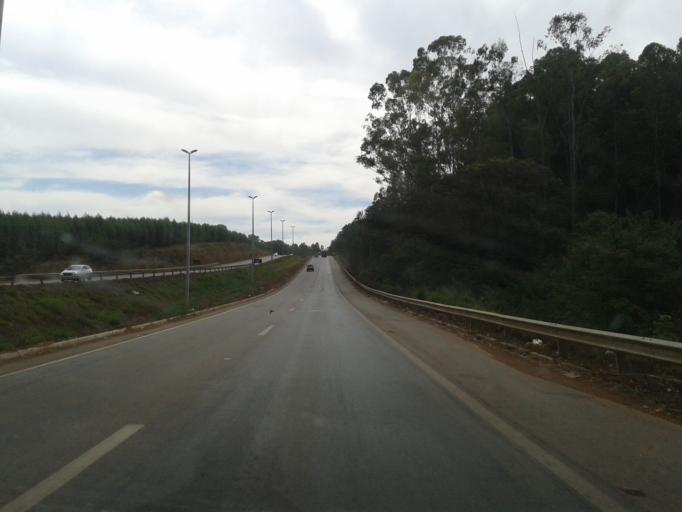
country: BR
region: Goias
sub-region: Inhumas
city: Inhumas
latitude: -16.3349
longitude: -49.5173
